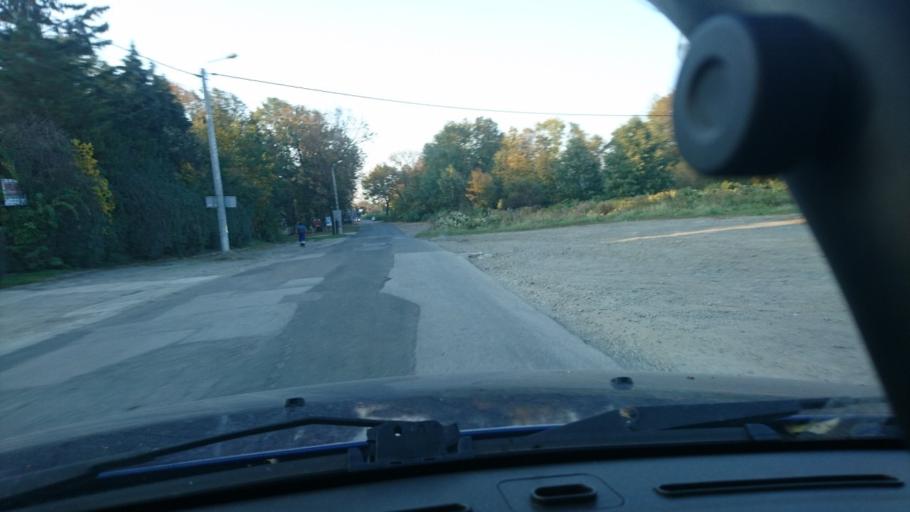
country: PL
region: Silesian Voivodeship
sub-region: Powiat bielski
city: Jaworze
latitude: 49.8169
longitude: 18.9820
